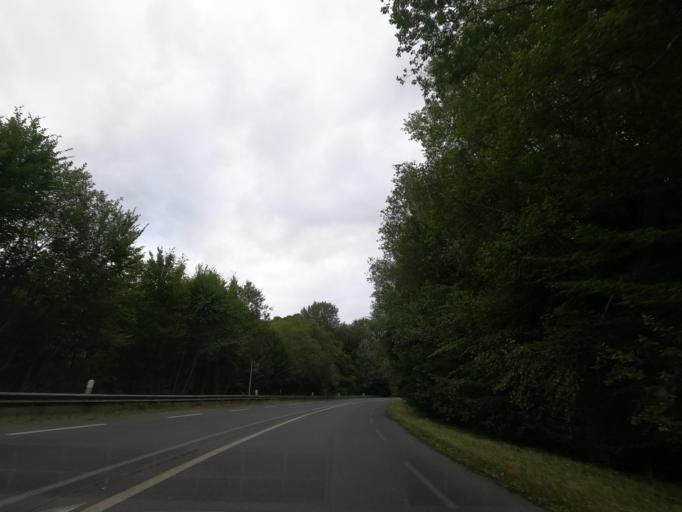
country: FR
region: Haute-Normandie
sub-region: Departement de la Seine-Maritime
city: Sahurs
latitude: 49.3405
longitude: 0.9249
